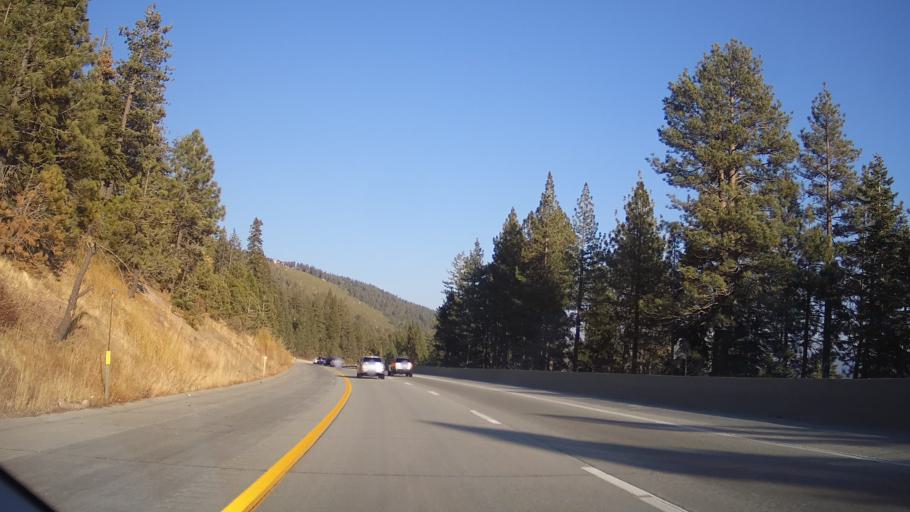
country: US
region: California
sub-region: Nevada County
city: Truckee
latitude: 39.3275
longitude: -120.2716
